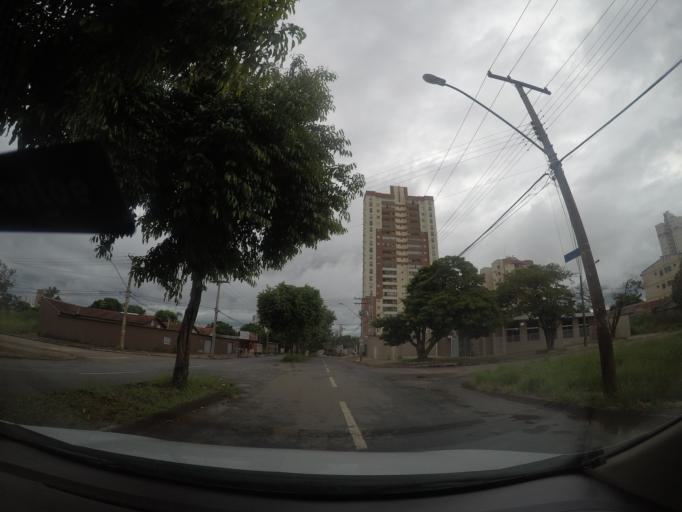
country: BR
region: Goias
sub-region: Goiania
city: Goiania
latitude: -16.7321
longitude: -49.2854
